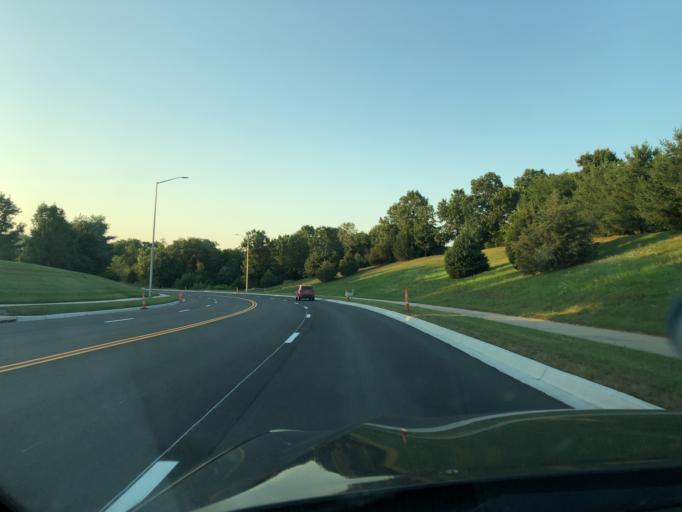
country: US
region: Kansas
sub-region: Leavenworth County
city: Leavenworth
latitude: 39.2792
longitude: -94.9462
